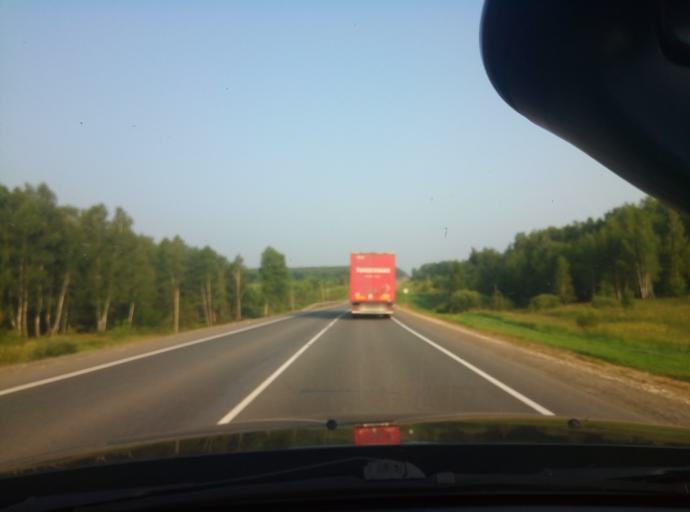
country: RU
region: Tula
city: Dubna
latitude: 54.3033
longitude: 37.0367
